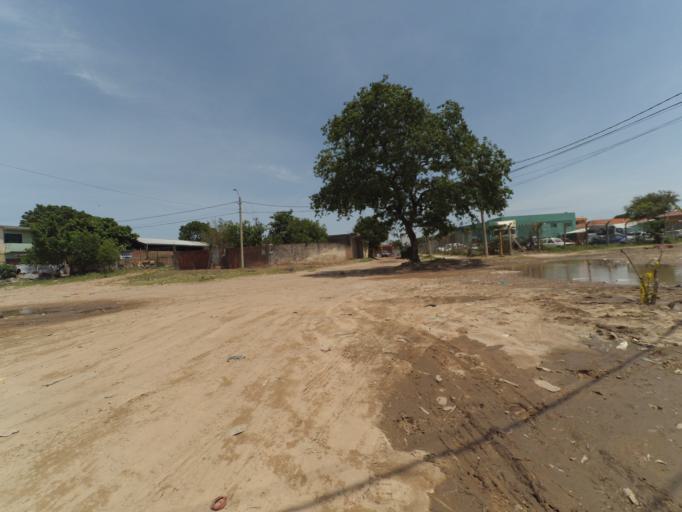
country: BO
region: Santa Cruz
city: Santa Cruz de la Sierra
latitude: -17.8303
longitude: -63.2384
